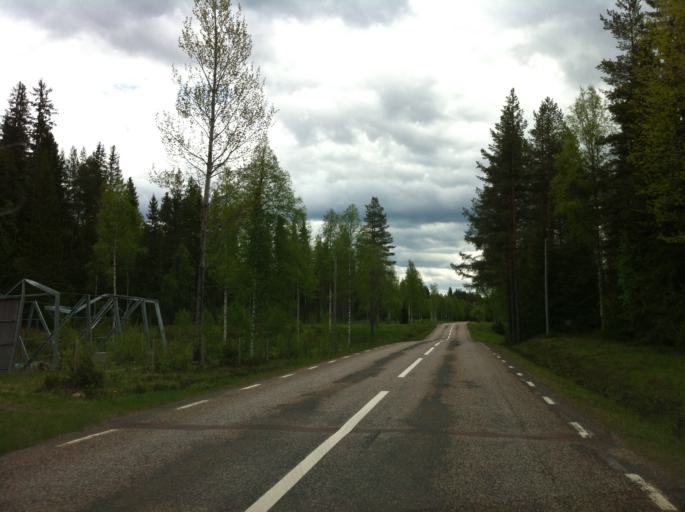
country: SE
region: Dalarna
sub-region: Malung-Saelens kommun
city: Malung
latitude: 61.2385
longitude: 13.2148
